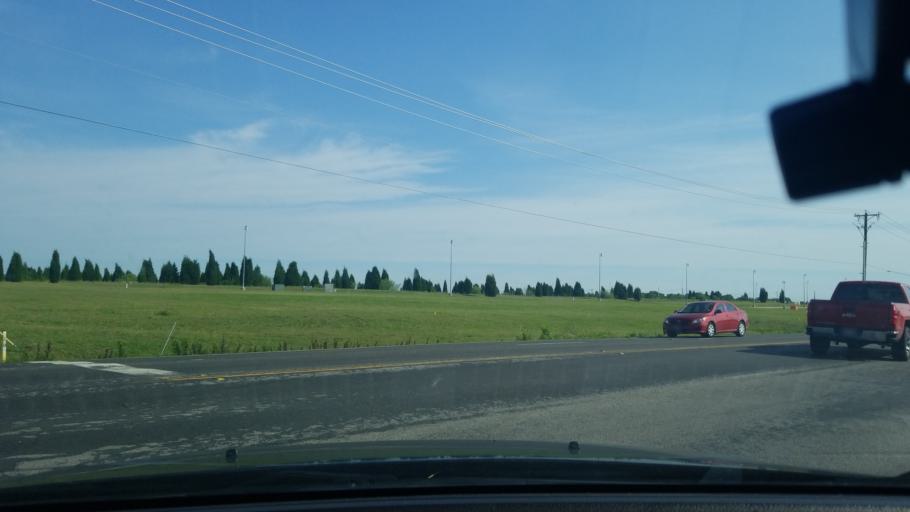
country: US
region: Texas
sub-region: Dallas County
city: Sunnyvale
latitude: 32.7795
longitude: -96.5660
